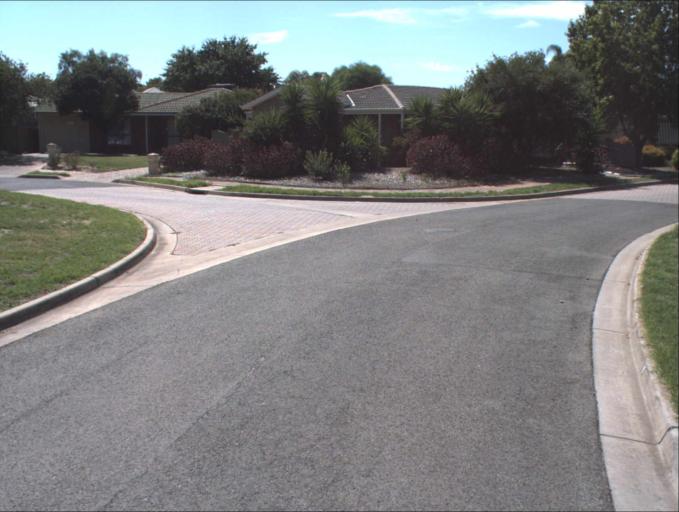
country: AU
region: South Australia
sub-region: Port Adelaide Enfield
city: Klemzig
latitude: -34.8805
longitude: 138.6445
